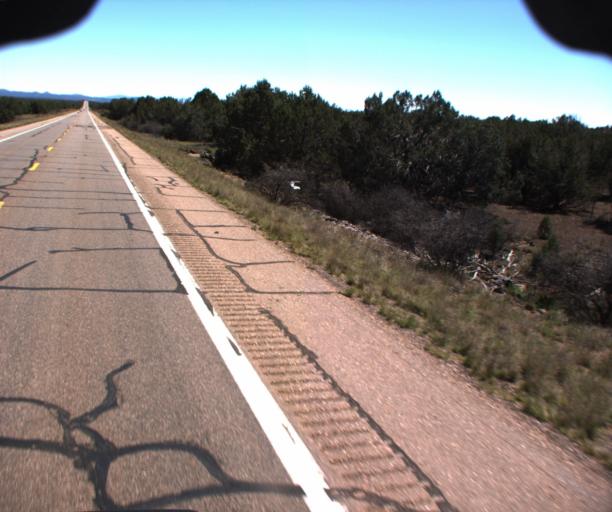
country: US
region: Arizona
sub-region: Yavapai County
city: Paulden
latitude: 35.0289
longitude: -112.3940
